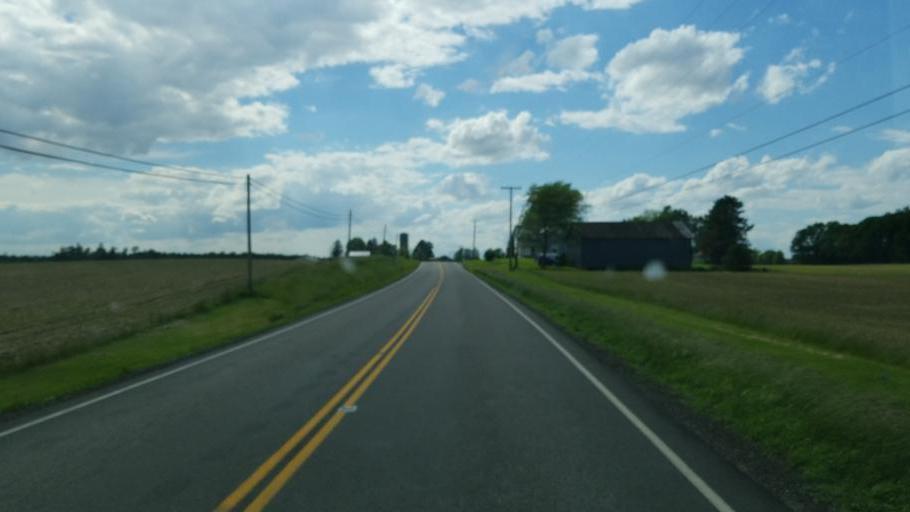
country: US
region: Ohio
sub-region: Huron County
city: Plymouth
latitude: 40.9696
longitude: -82.6113
